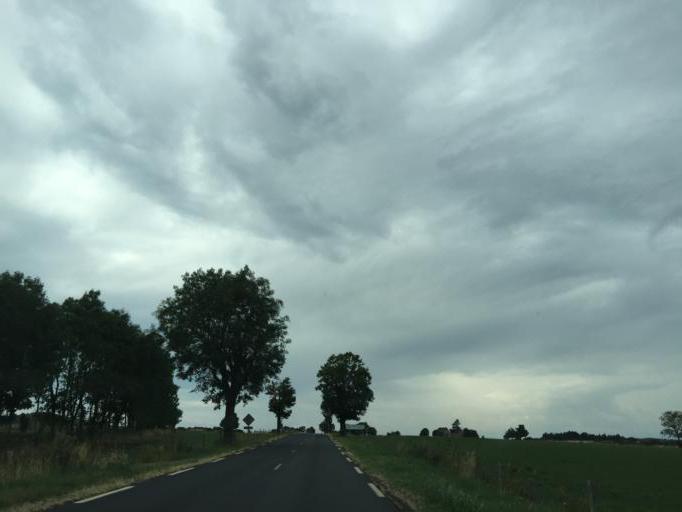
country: FR
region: Auvergne
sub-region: Departement de la Haute-Loire
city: Solignac-sur-Loire
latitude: 44.8616
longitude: 3.8465
